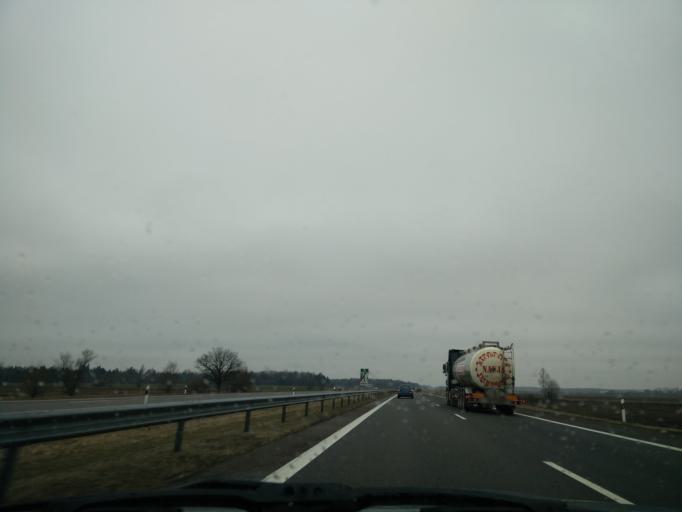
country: LT
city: Raseiniai
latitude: 55.3701
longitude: 22.9670
